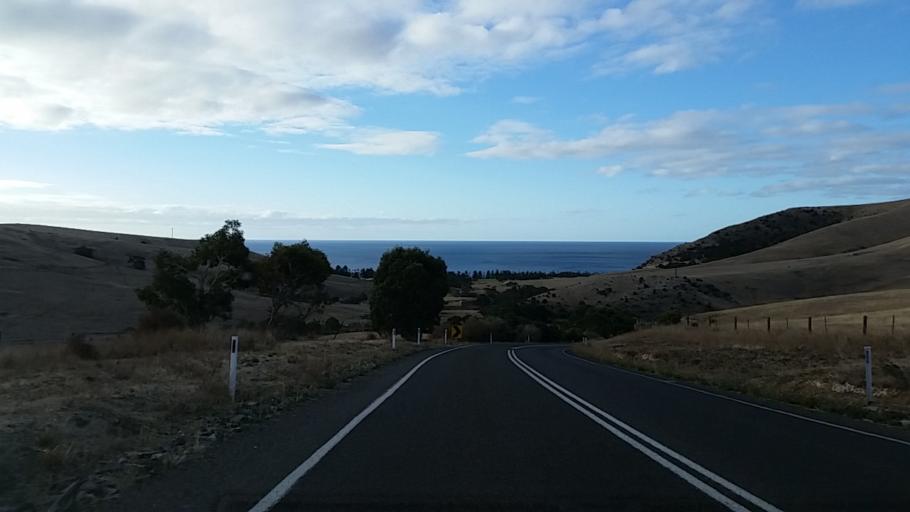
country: AU
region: South Australia
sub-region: Yankalilla
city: Normanville
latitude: -35.5389
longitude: 138.1940
